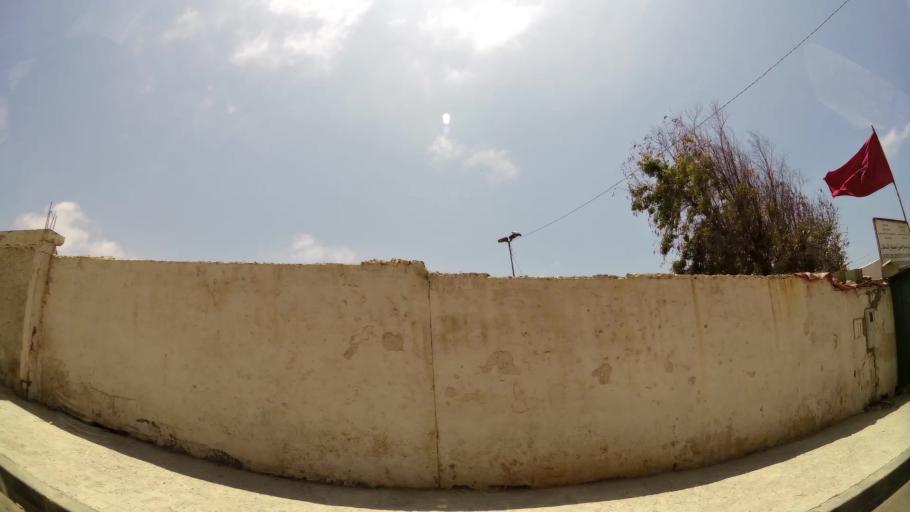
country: MA
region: Rabat-Sale-Zemmour-Zaer
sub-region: Rabat
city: Rabat
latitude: 34.0096
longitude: -6.8654
